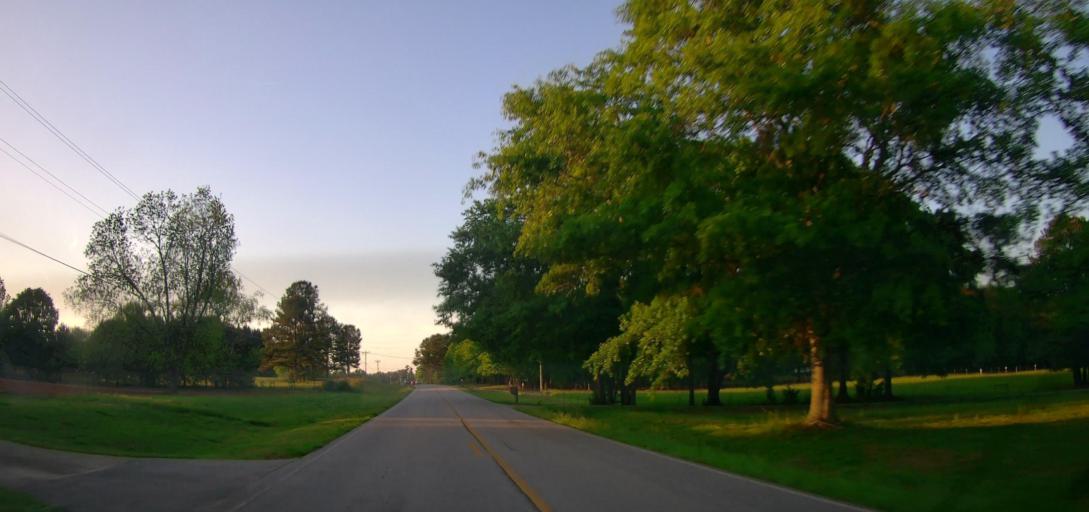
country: US
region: Georgia
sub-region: Henry County
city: McDonough
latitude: 33.4242
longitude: -84.0906
